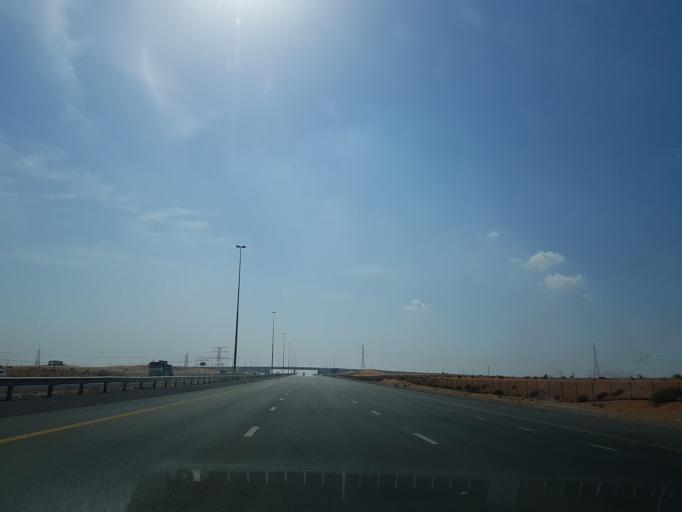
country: AE
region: Ra's al Khaymah
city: Ras al-Khaimah
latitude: 25.6998
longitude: 55.9311
